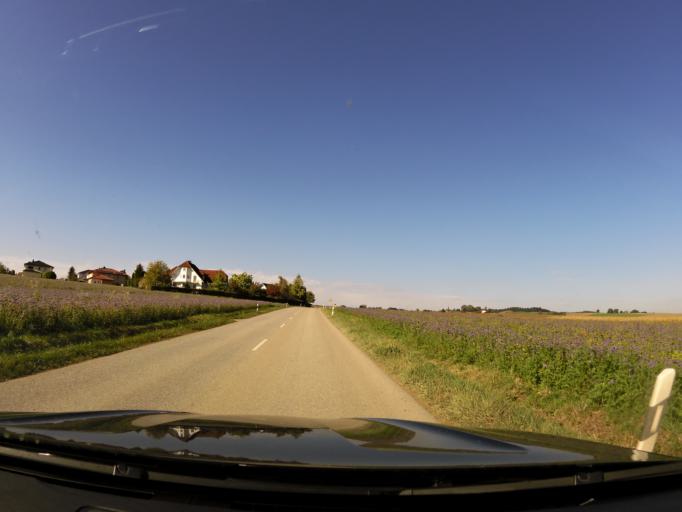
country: DE
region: Bavaria
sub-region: Lower Bavaria
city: Tiefenbach
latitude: 48.4888
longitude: 12.1025
